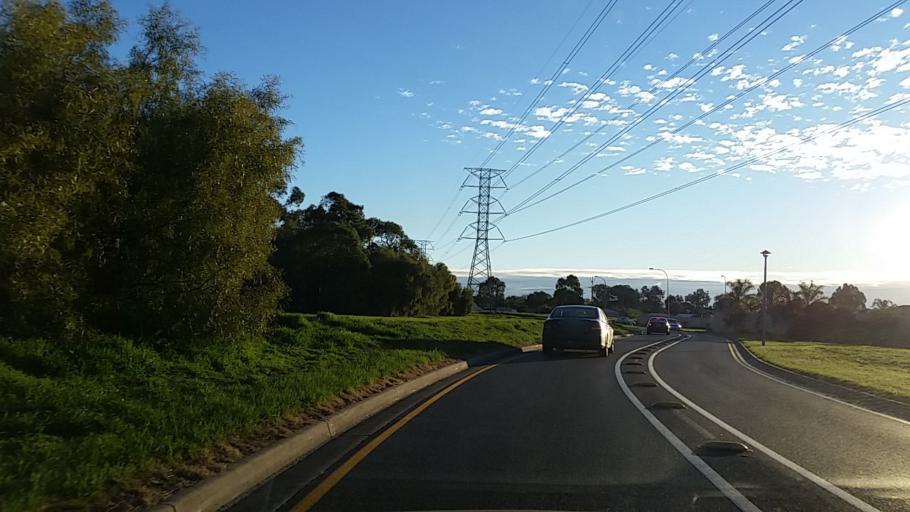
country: AU
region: South Australia
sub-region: Salisbury
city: Salisbury
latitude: -34.7607
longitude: 138.6220
